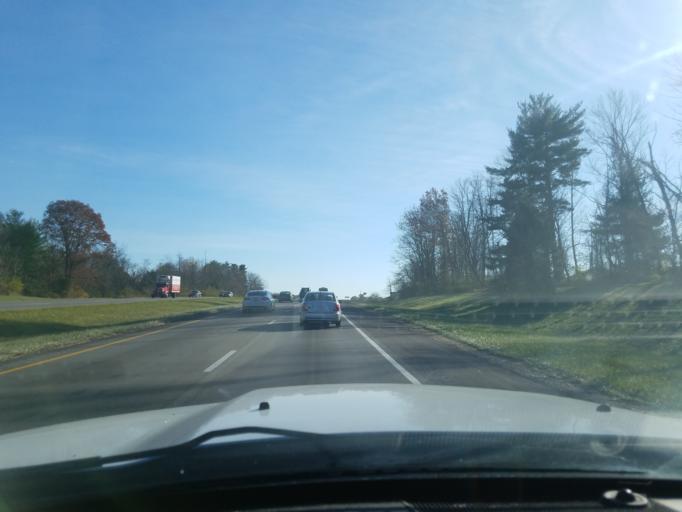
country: US
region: Ohio
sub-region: Clermont County
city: Batavia
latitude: 39.0854
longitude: -84.1591
